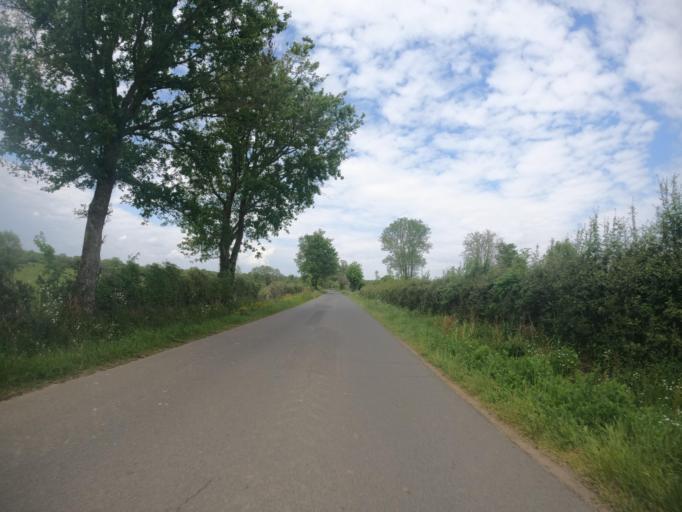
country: FR
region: Poitou-Charentes
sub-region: Departement des Deux-Sevres
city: Saint-Varent
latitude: 46.8762
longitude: -0.2959
